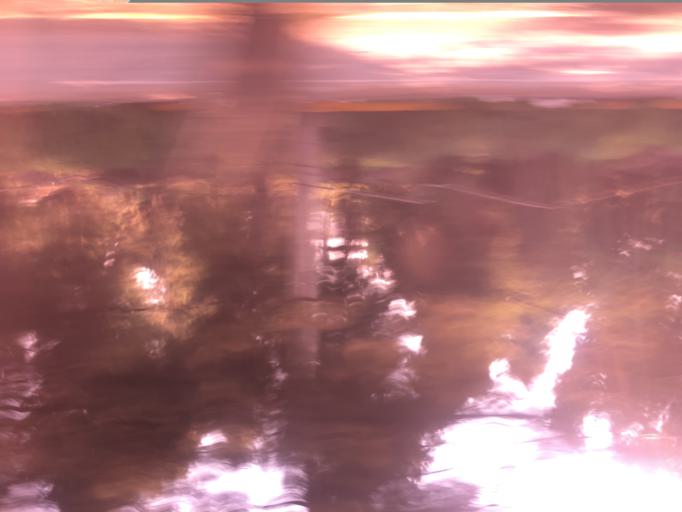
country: MX
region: Mexico
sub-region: Ciudad Nezahualcoyotl
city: Colonia Gustavo Baz Prada
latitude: 19.4731
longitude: -98.9930
